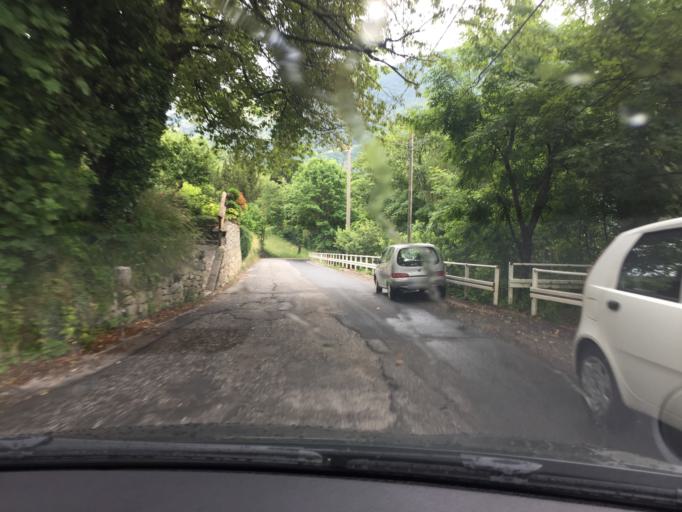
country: IT
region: Lombardy
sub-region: Provincia di Lecco
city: Esino Lario
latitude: 45.9970
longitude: 9.3403
